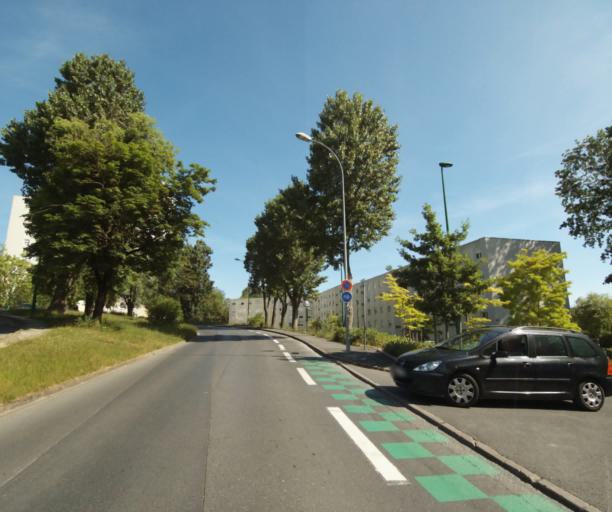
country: FR
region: Champagne-Ardenne
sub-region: Departement des Ardennes
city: La Francheville
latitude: 49.7422
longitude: 4.7231
